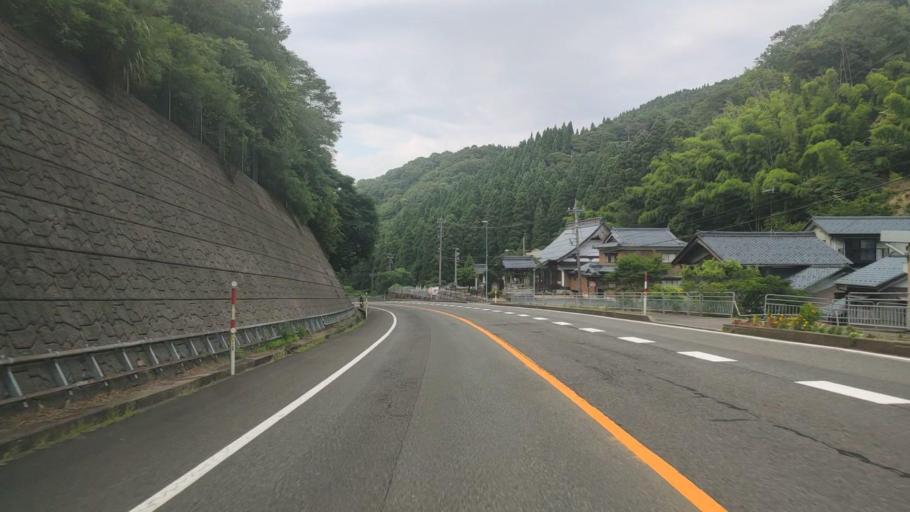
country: JP
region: Fukui
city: Takefu
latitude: 35.8041
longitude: 136.0940
